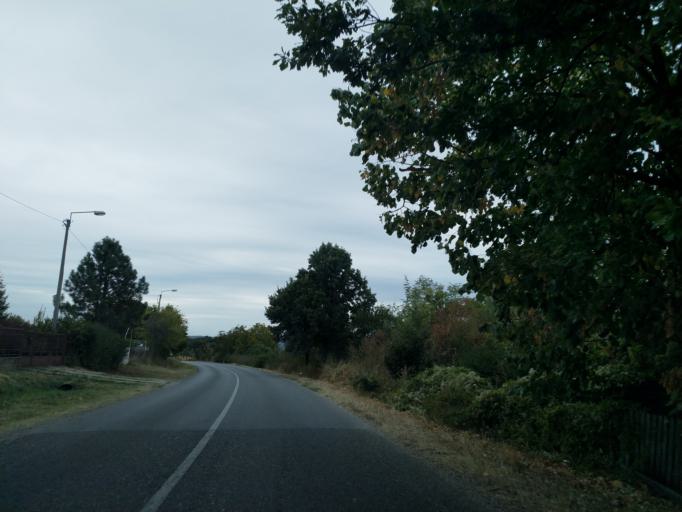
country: RS
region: Central Serbia
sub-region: Pomoravski Okrug
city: Jagodina
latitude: 44.0082
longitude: 21.2029
